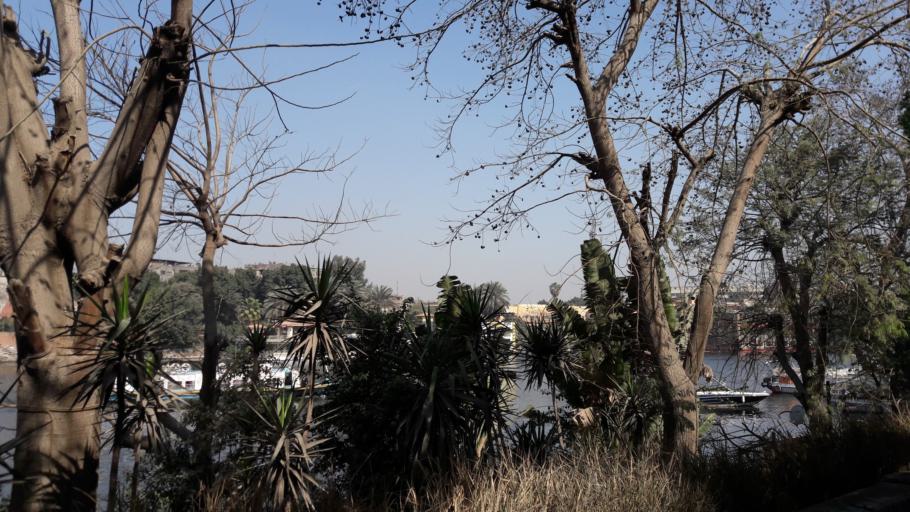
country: EG
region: Muhafazat al Qahirah
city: Cairo
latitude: 30.0723
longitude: 31.2210
